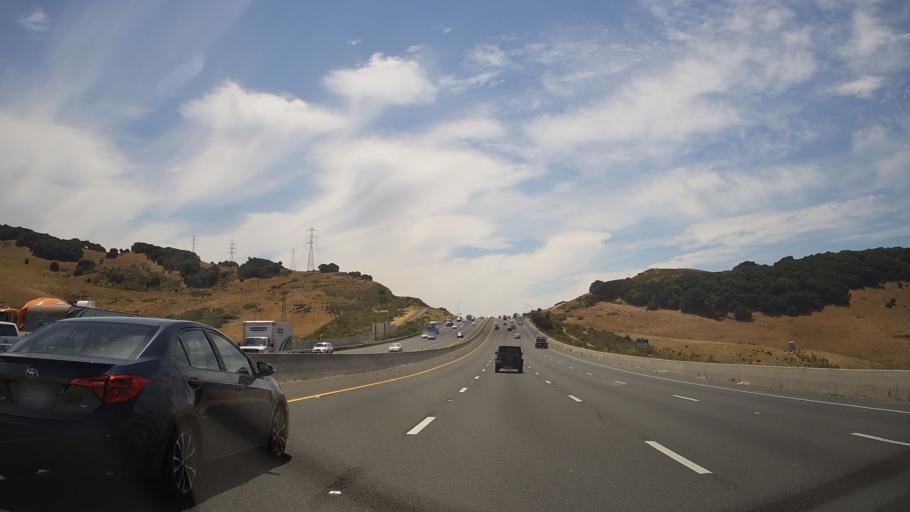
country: US
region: California
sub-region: Napa County
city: American Canyon
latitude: 38.1613
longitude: -122.2111
